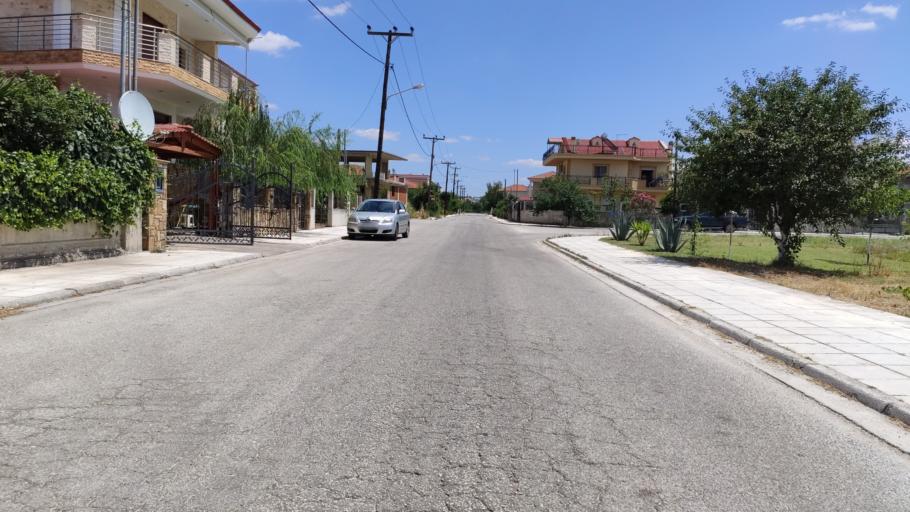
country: GR
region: East Macedonia and Thrace
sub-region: Nomos Rodopis
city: Komotini
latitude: 41.1303
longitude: 25.3985
